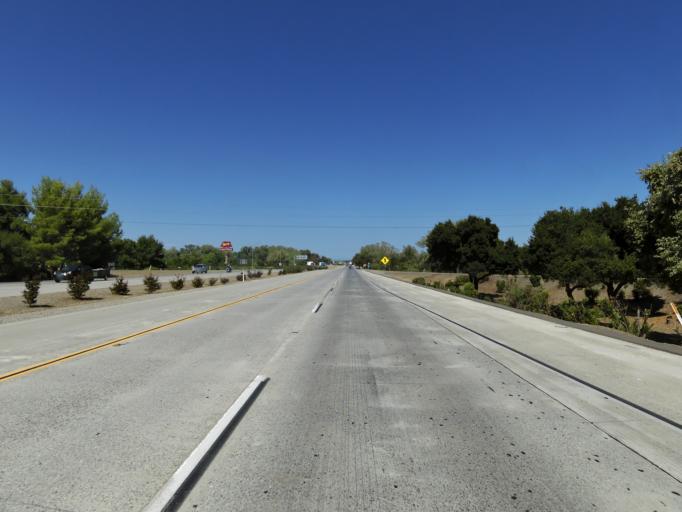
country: US
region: California
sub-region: Tehama County
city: Red Bluff
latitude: 40.1815
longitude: -122.2257
